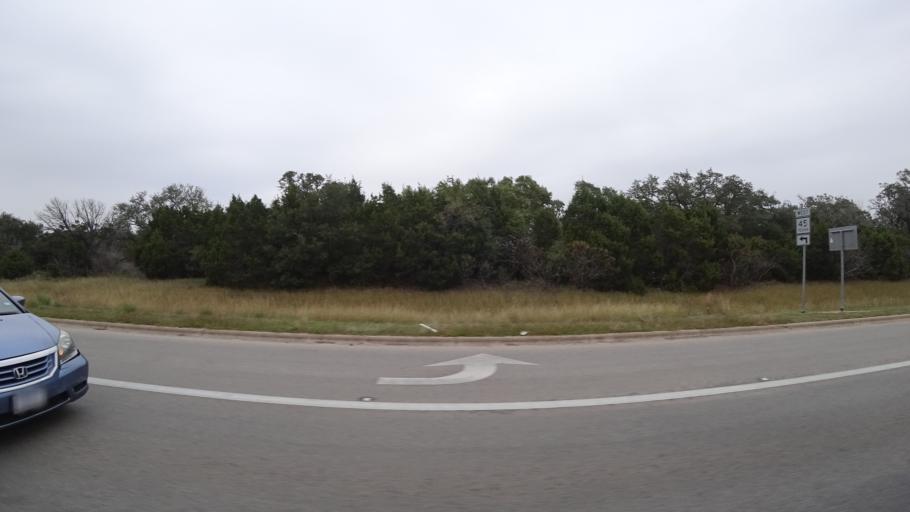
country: US
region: Texas
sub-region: Travis County
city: Shady Hollow
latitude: 30.1816
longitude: -97.9014
